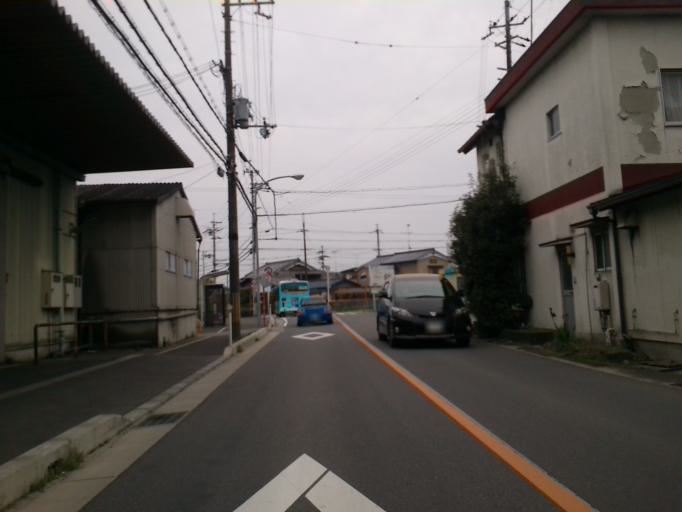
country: JP
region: Kyoto
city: Tanabe
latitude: 34.8407
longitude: 135.7418
